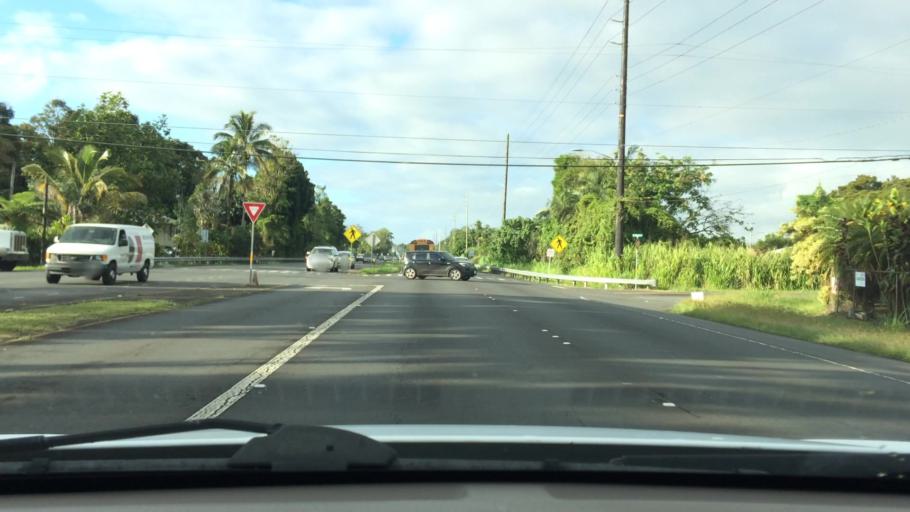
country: US
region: Hawaii
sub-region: Hawaii County
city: Hilo
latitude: 19.6802
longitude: -155.0652
